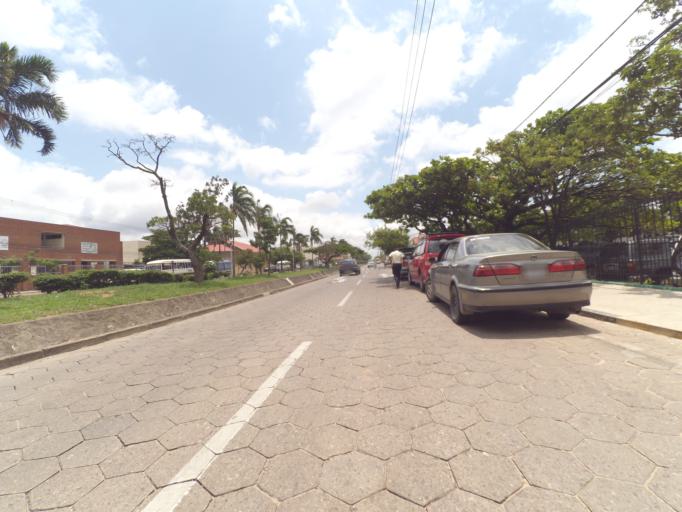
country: BO
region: Santa Cruz
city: Santa Cruz de la Sierra
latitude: -17.7853
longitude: -63.2013
